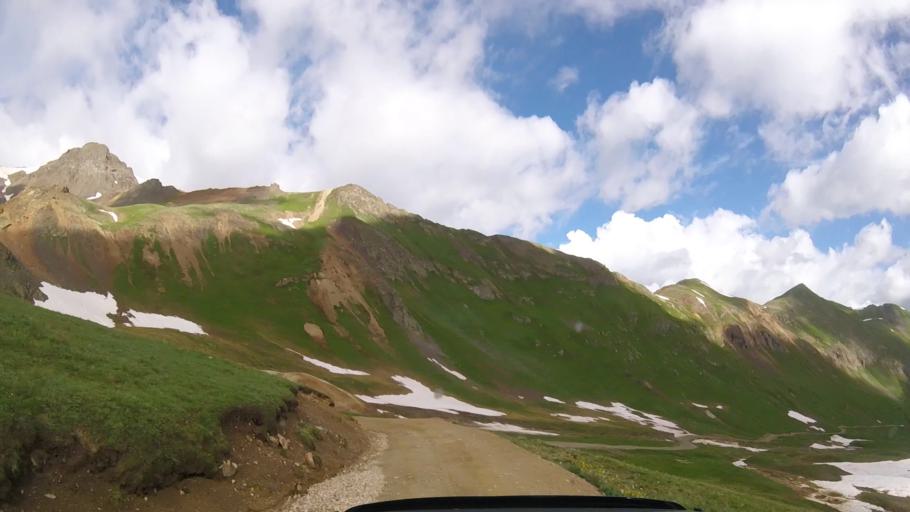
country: US
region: Colorado
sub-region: San Juan County
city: Silverton
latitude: 37.9160
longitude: -107.6122
